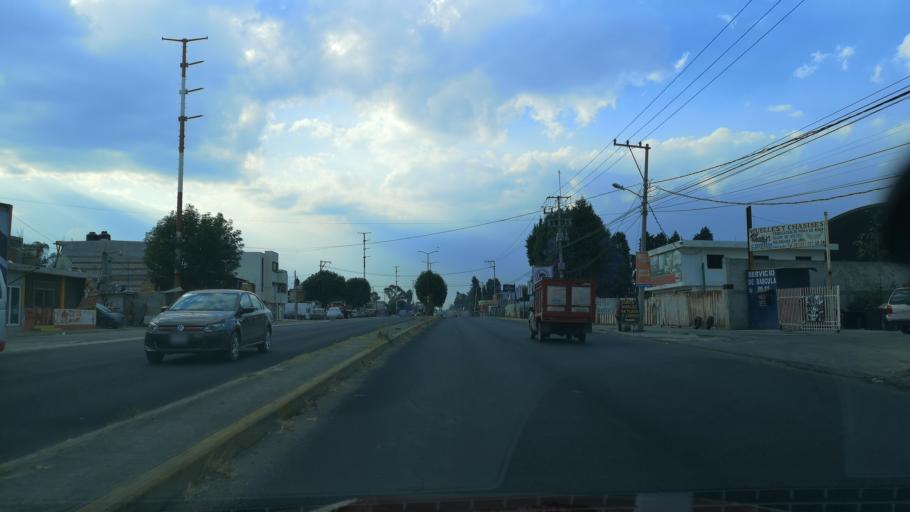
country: MX
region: Puebla
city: Cuanala
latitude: 19.1055
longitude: -98.3496
